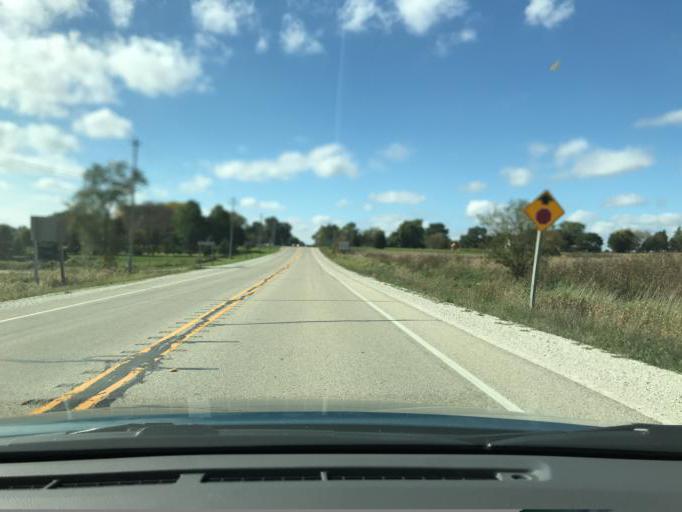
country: US
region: Wisconsin
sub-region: Racine County
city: Union Grove
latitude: 42.6337
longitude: -88.0472
